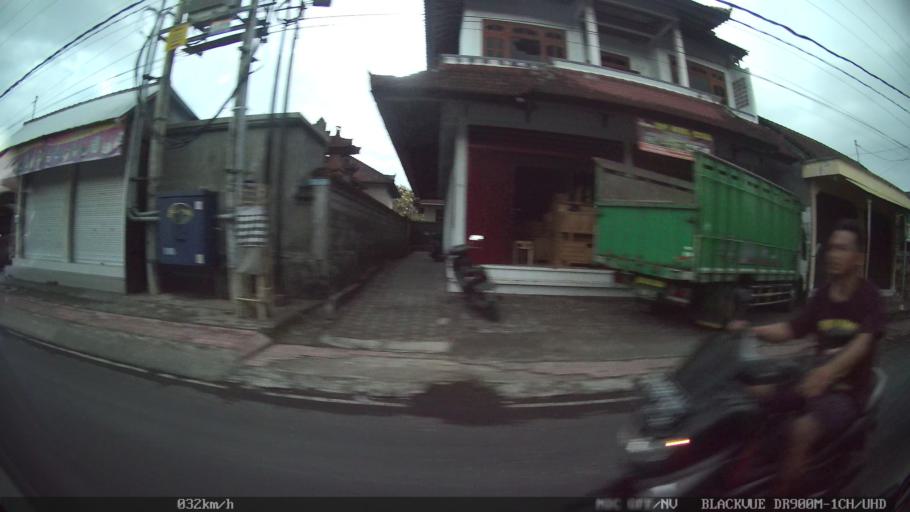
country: ID
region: Bali
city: Banjar Pasekan
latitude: -8.6209
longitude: 115.2839
